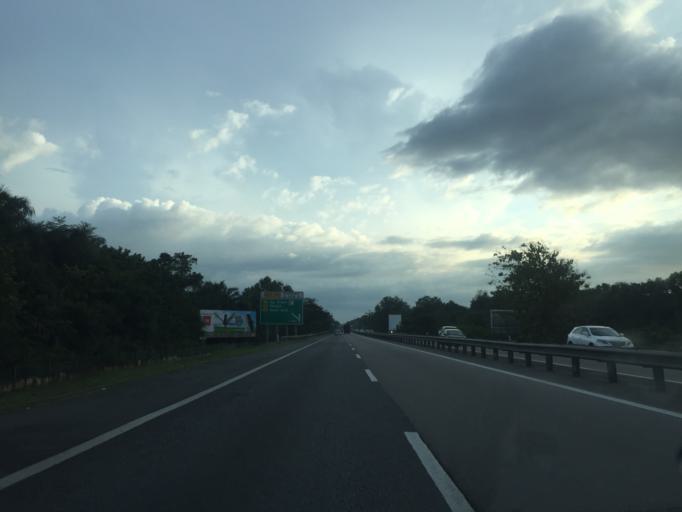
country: MY
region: Kedah
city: Bedong
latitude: 5.6857
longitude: 100.5191
